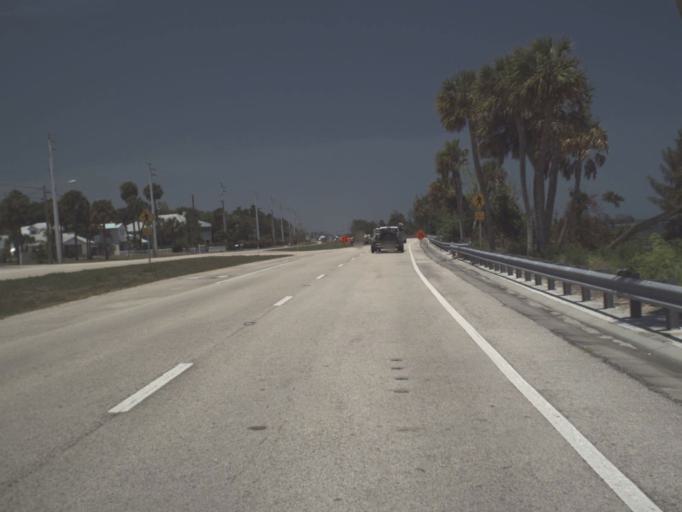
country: US
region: Florida
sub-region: Brevard County
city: Micco
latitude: 27.8745
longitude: -80.4980
